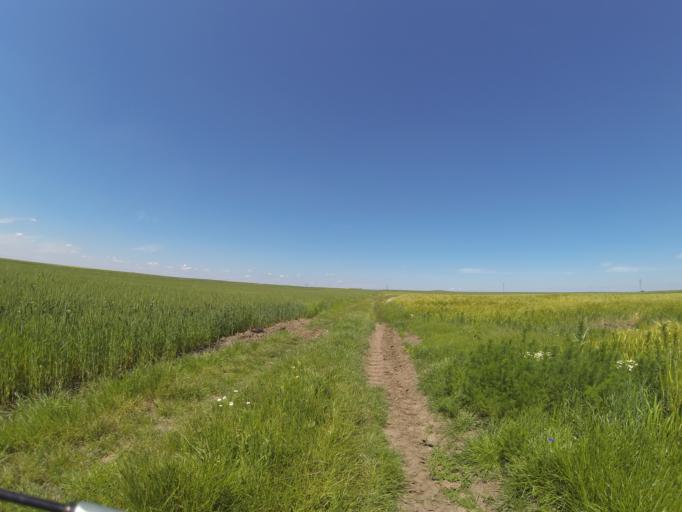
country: RO
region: Dolj
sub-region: Comuna Leu
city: Leu
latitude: 44.2035
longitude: 24.0324
